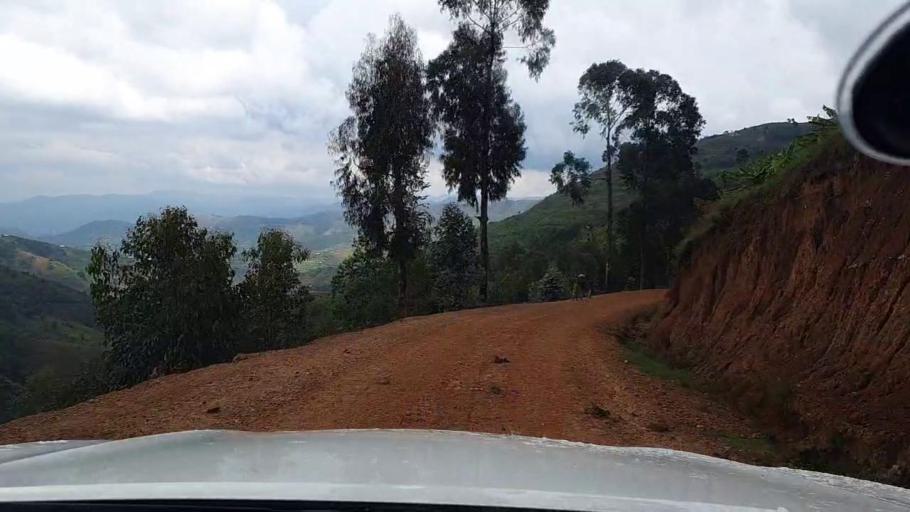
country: RW
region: Western Province
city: Kibuye
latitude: -2.1464
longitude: 29.4248
